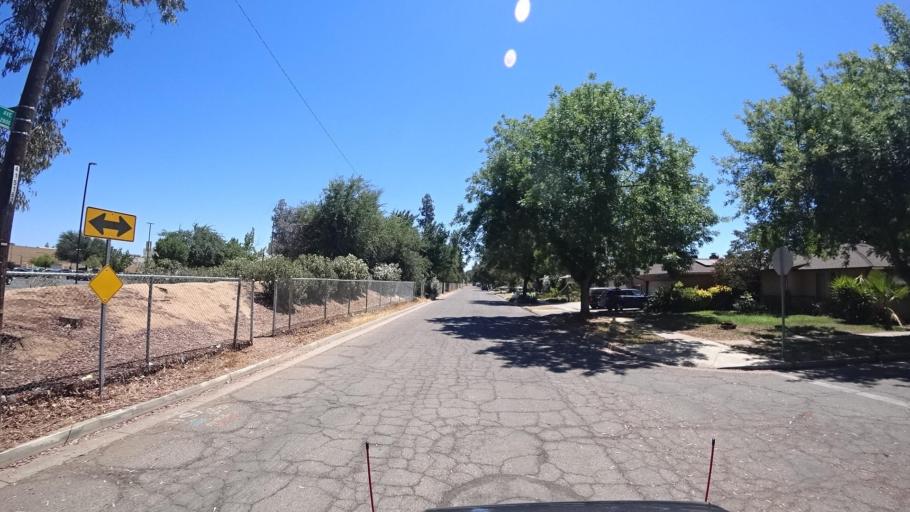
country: US
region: California
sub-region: Fresno County
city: Fresno
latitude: 36.8049
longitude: -119.7781
